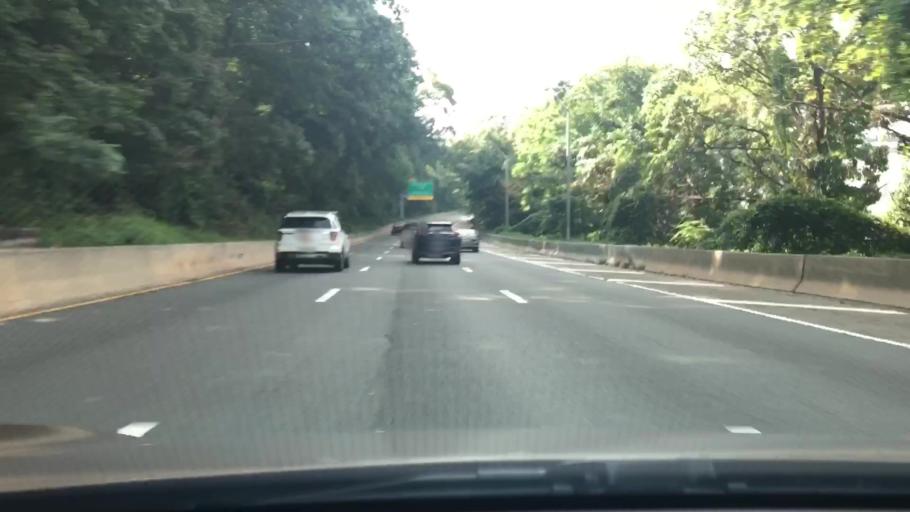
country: US
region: New York
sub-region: New York County
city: Inwood
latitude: 40.8544
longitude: -73.9409
